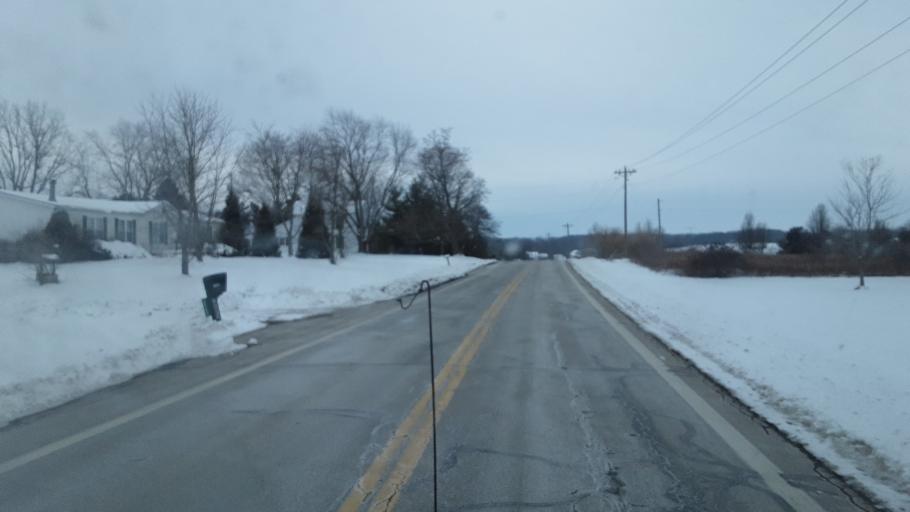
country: US
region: Ohio
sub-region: Champaign County
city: Mechanicsburg
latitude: 40.0980
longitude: -83.5761
